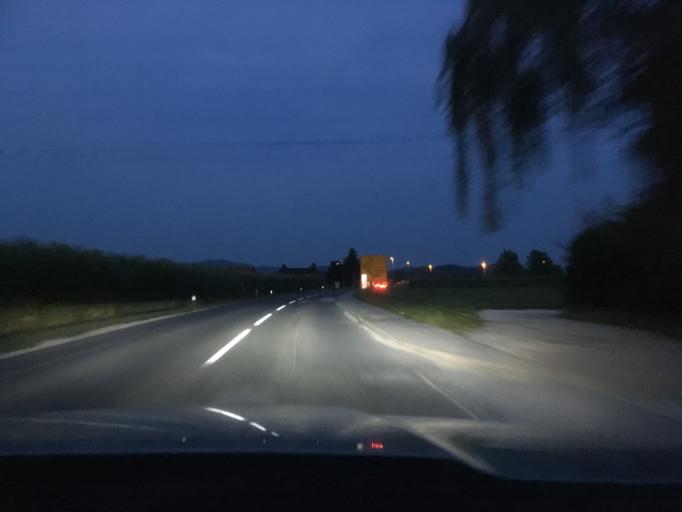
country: SI
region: Kamnik
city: Smarca
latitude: 46.1991
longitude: 14.5885
